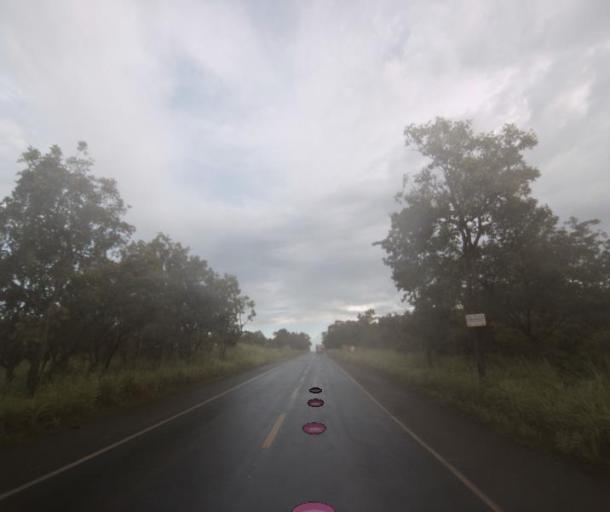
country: BR
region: Goias
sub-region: Porangatu
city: Porangatu
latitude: -13.8191
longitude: -49.0410
